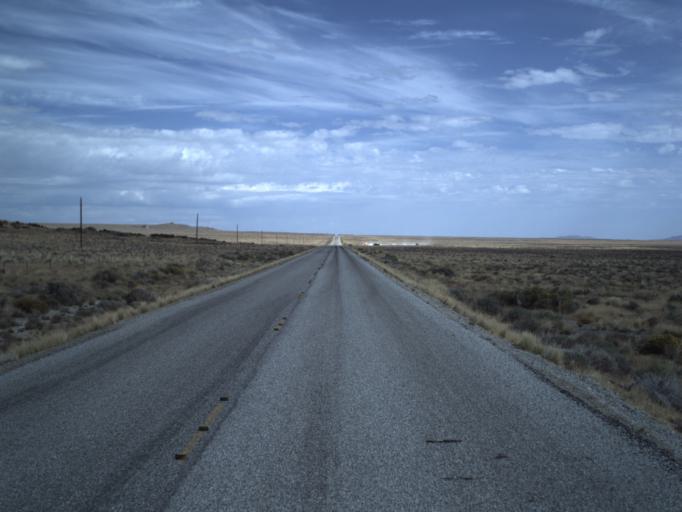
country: US
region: Utah
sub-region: Tooele County
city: Wendover
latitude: 41.4603
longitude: -113.6521
